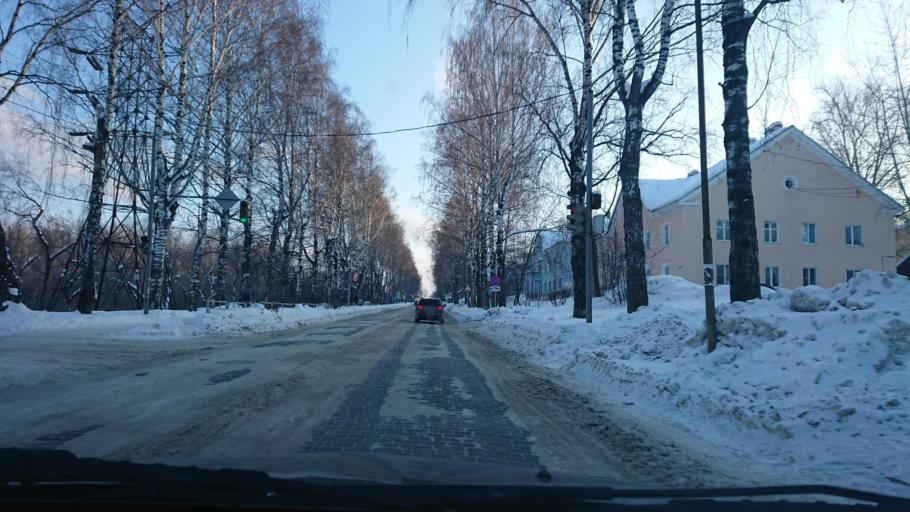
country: RU
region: Sverdlovsk
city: Degtyarsk
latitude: 56.6968
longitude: 60.0880
